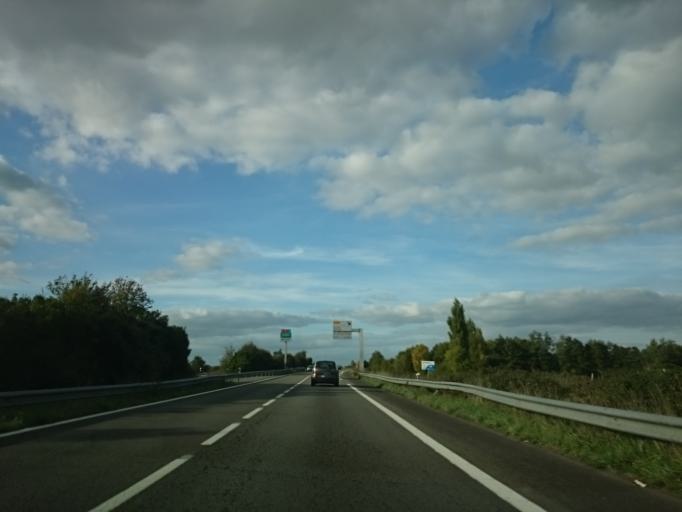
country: FR
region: Pays de la Loire
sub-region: Departement de la Loire-Atlantique
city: Heric
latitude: 47.4347
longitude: -1.6389
